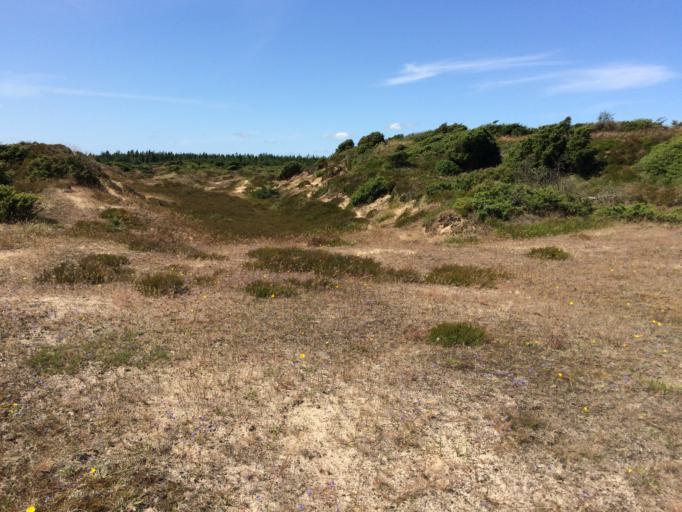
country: DK
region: Central Jutland
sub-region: Holstebro Kommune
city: Ulfborg
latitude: 56.2633
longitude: 8.4080
